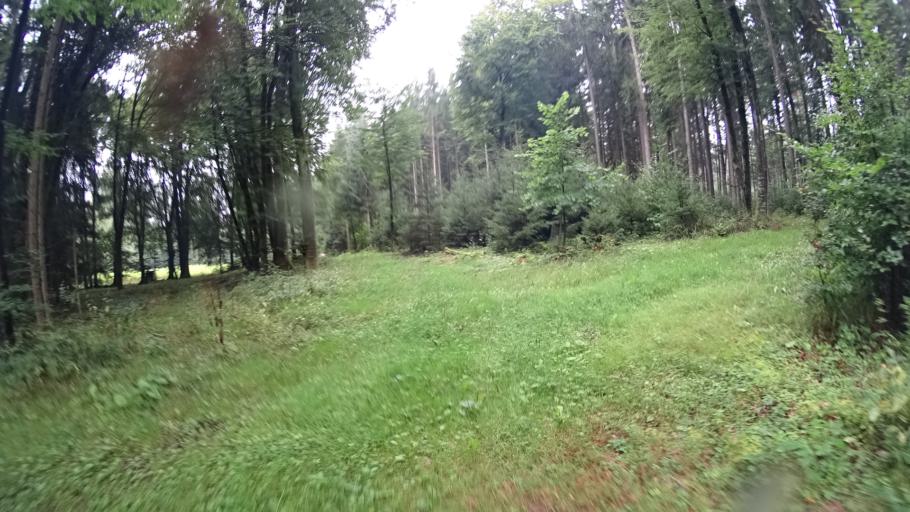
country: DE
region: Bavaria
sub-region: Upper Bavaria
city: Bohmfeld
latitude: 48.9132
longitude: 11.3904
